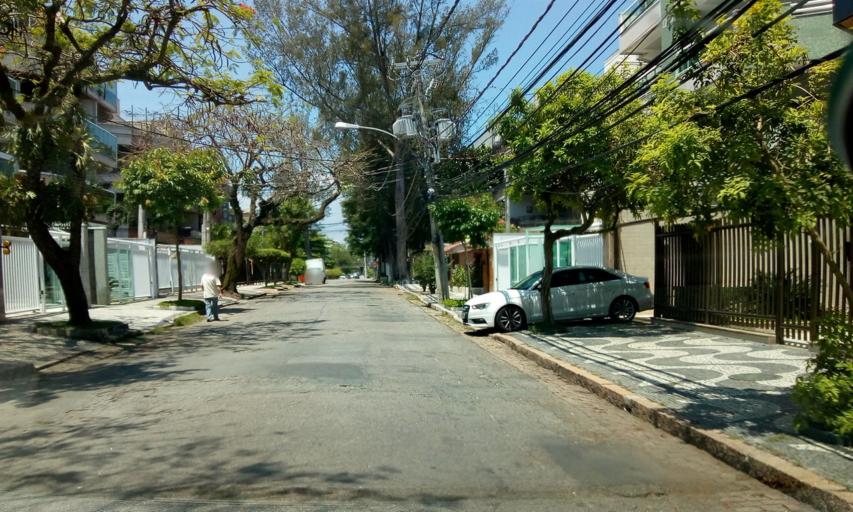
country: BR
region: Rio de Janeiro
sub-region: Nilopolis
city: Nilopolis
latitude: -23.0240
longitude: -43.4594
